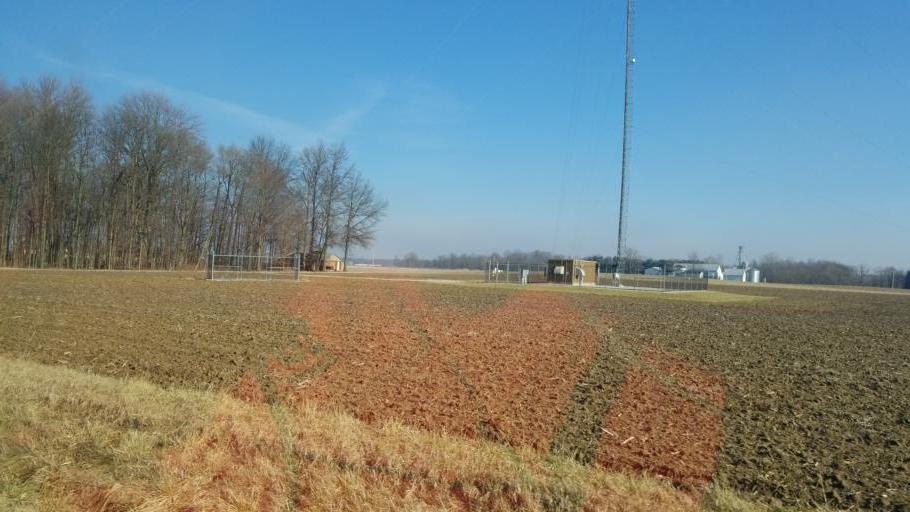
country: US
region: Ohio
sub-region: Crawford County
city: Bucyrus
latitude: 40.9548
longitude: -83.0742
